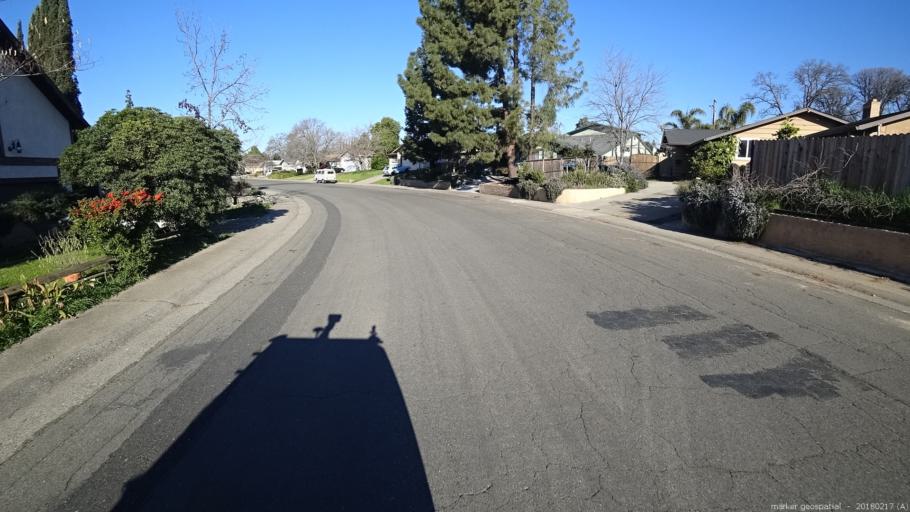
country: US
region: California
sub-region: Sacramento County
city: Folsom
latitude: 38.6713
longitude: -121.1923
